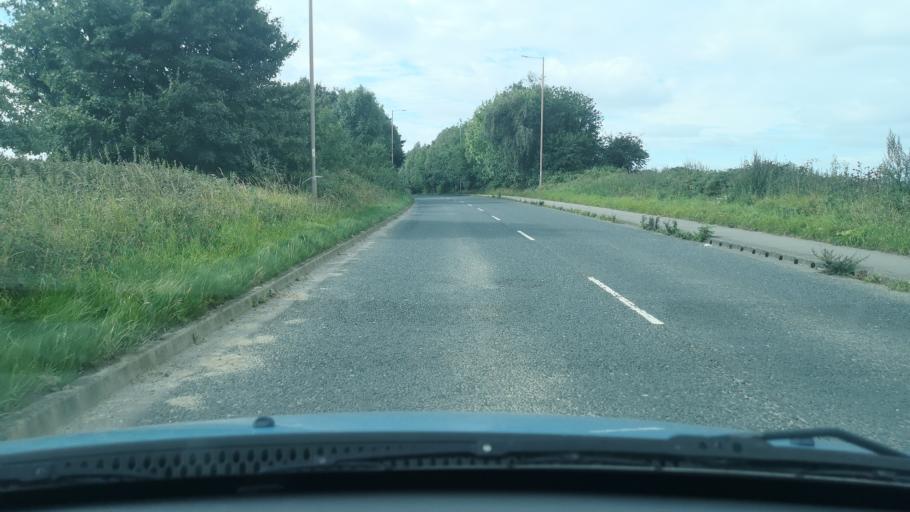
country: GB
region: England
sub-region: City and Borough of Wakefield
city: Hemsworth
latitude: 53.6036
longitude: -1.3731
